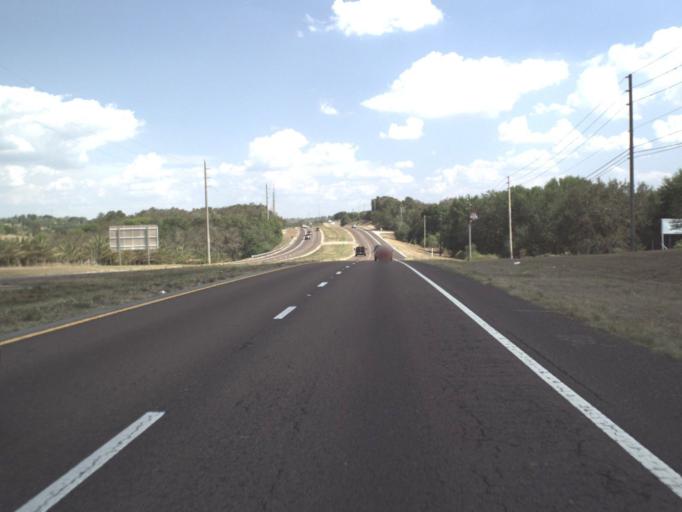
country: US
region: Florida
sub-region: Lake County
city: Minneola
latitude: 28.6345
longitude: -81.7794
